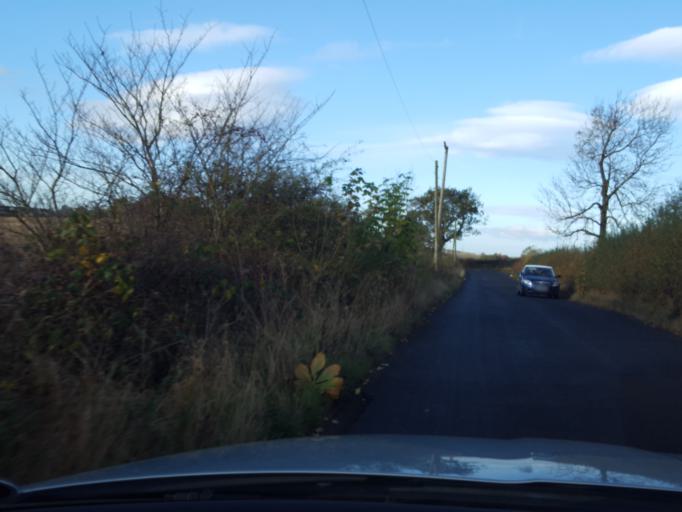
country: GB
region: Scotland
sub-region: North Lanarkshire
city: Chryston
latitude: 55.8751
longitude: -4.0898
